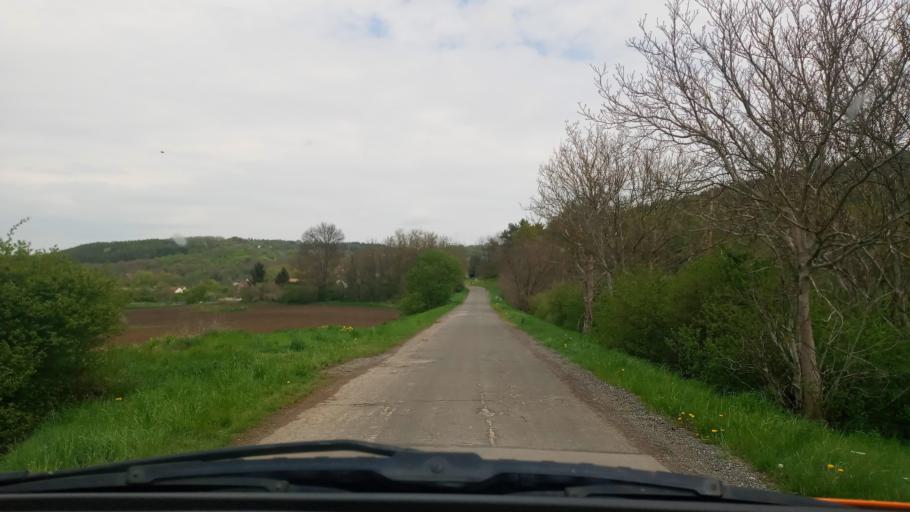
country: HU
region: Baranya
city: Sasd
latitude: 46.2613
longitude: 18.1202
